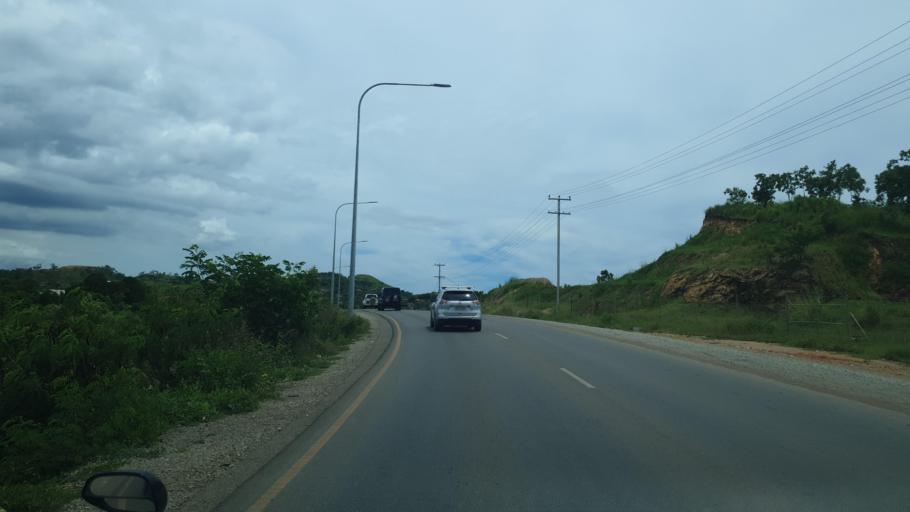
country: PG
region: National Capital
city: Port Moresby
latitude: -9.5035
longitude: 147.2354
